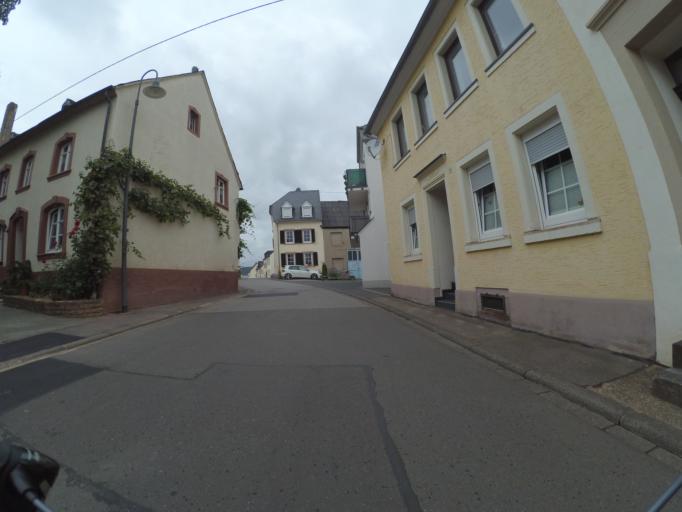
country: DE
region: Rheinland-Pfalz
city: Bekond
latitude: 49.8492
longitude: 6.8033
